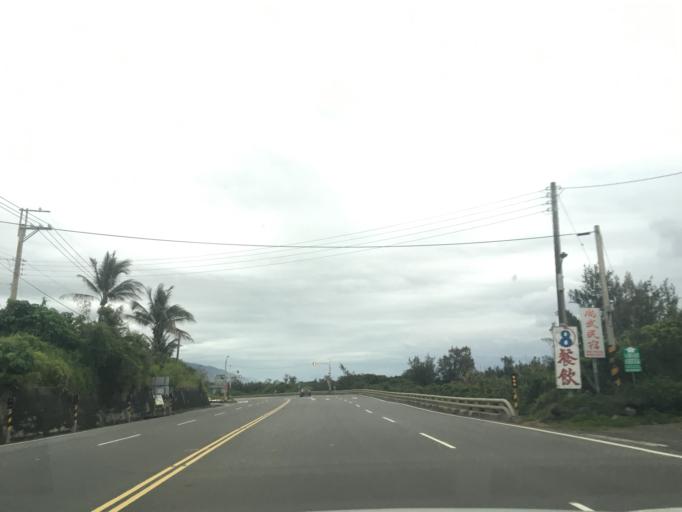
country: TW
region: Taiwan
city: Hengchun
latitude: 22.3039
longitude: 120.8893
